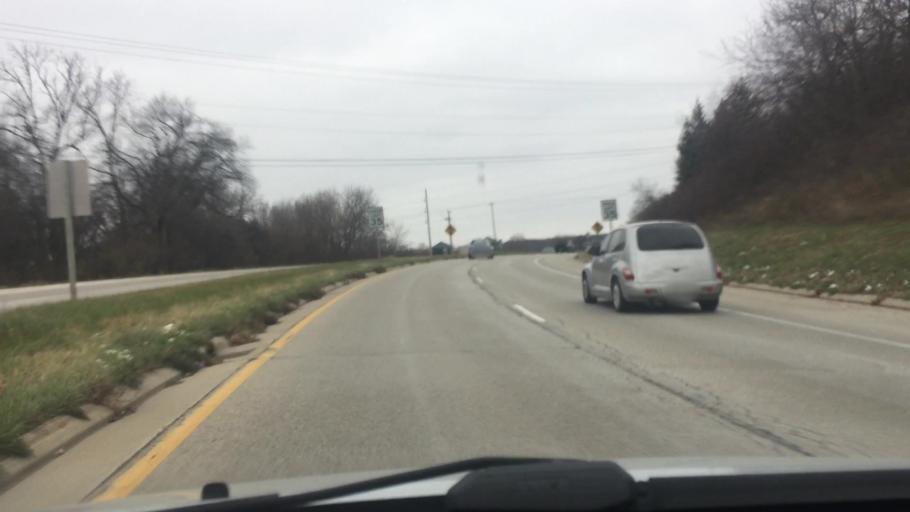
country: US
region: Wisconsin
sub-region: Waukesha County
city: Delafield
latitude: 43.0569
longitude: -88.3691
